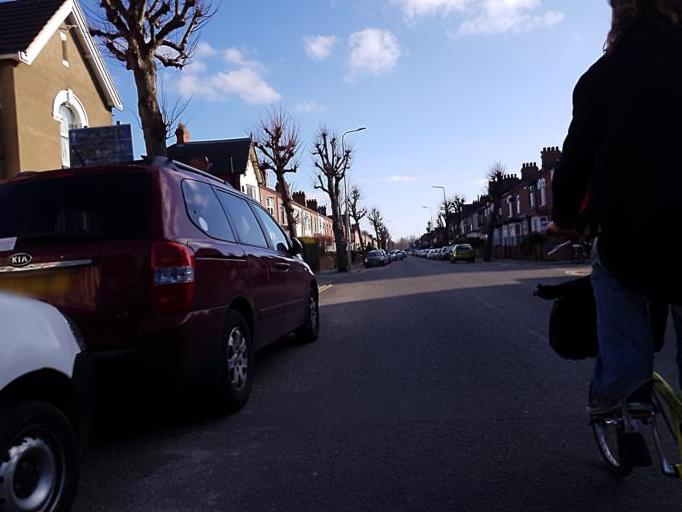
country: GB
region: England
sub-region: North East Lincolnshire
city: Grimsby
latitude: 53.5577
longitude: -0.0758
